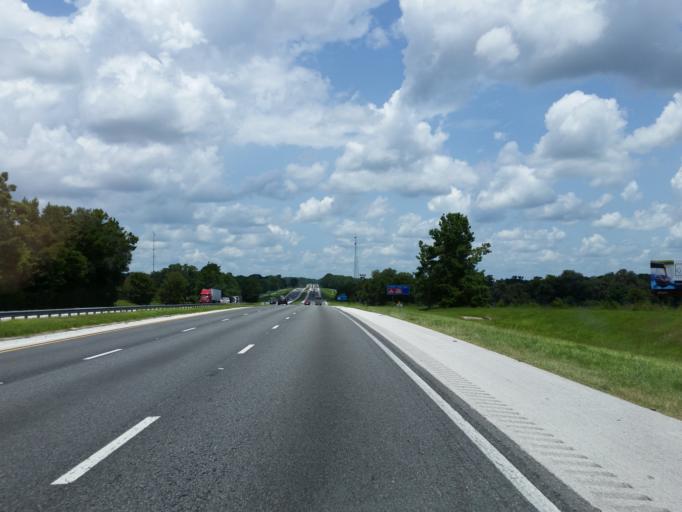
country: US
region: Florida
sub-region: Marion County
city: Citra
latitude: 29.3992
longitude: -82.2417
